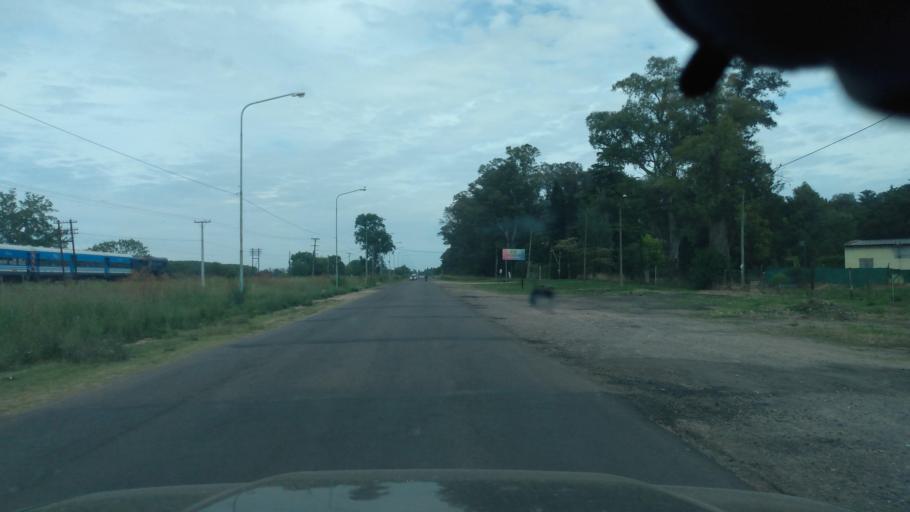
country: AR
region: Buenos Aires
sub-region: Partido de Lujan
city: Lujan
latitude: -34.5809
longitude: -59.0711
